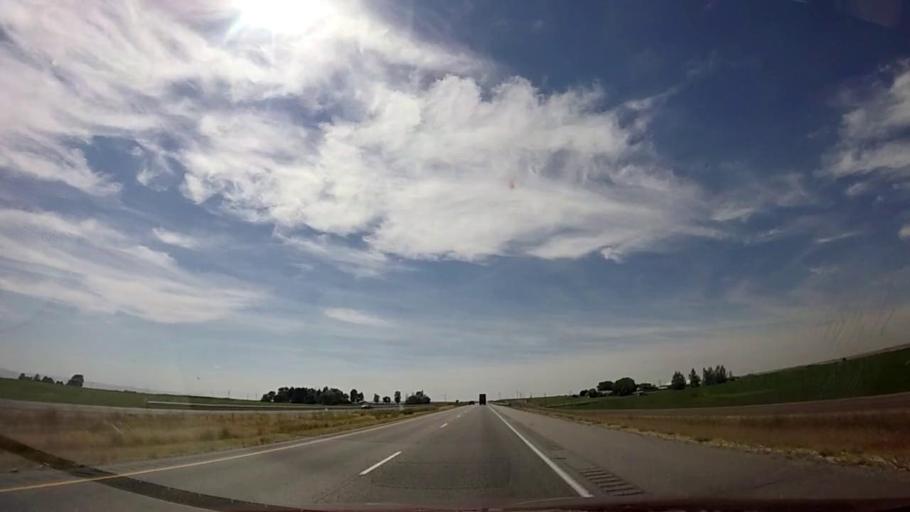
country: US
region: Idaho
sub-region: Cassia County
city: Burley
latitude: 42.5764
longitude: -113.9862
